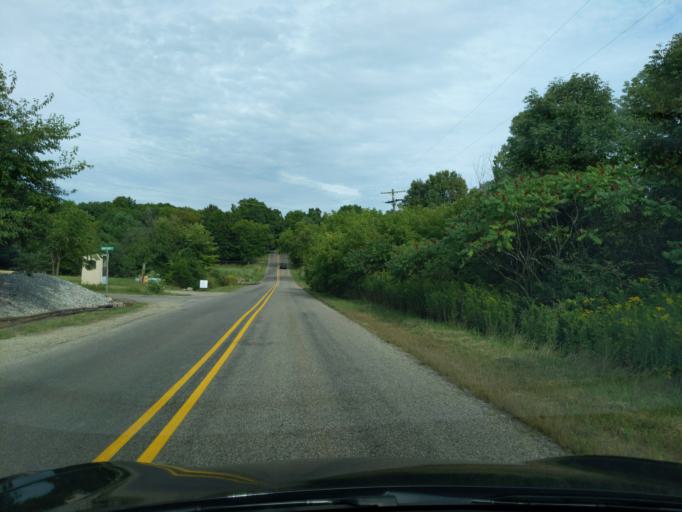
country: US
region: Michigan
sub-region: Eaton County
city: Dimondale
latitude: 42.6691
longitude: -84.6363
